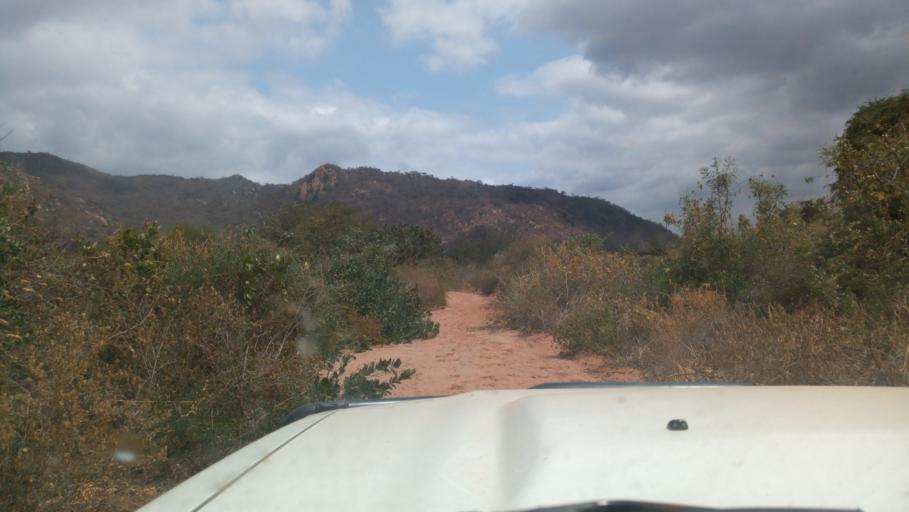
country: KE
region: Kitui
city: Kitui
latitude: -1.8712
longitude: 38.3640
